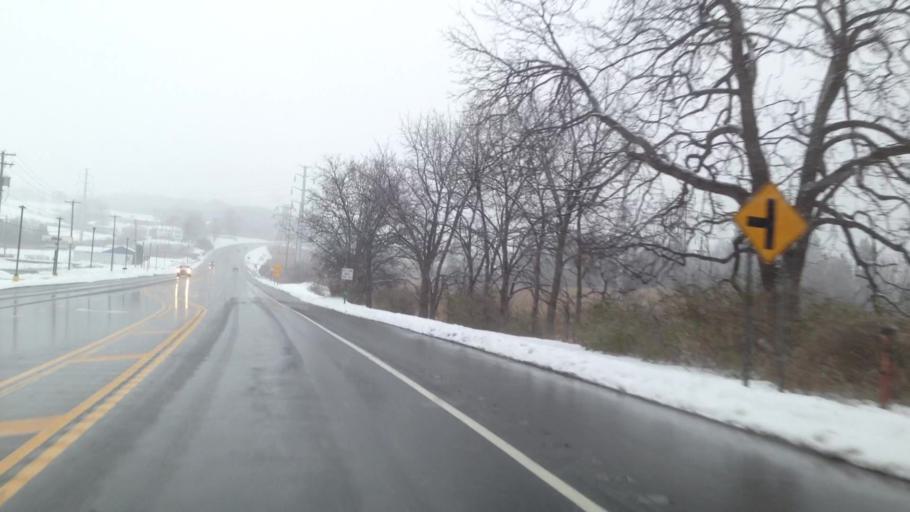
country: US
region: New York
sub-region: Onondaga County
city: Elbridge
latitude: 43.0375
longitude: -76.4050
